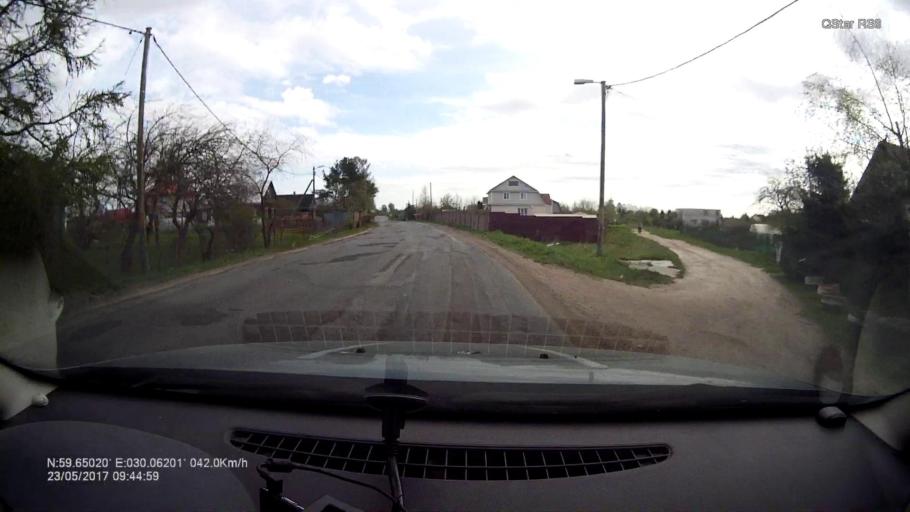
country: RU
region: Leningrad
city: Taytsy
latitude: 59.6502
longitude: 30.0621
